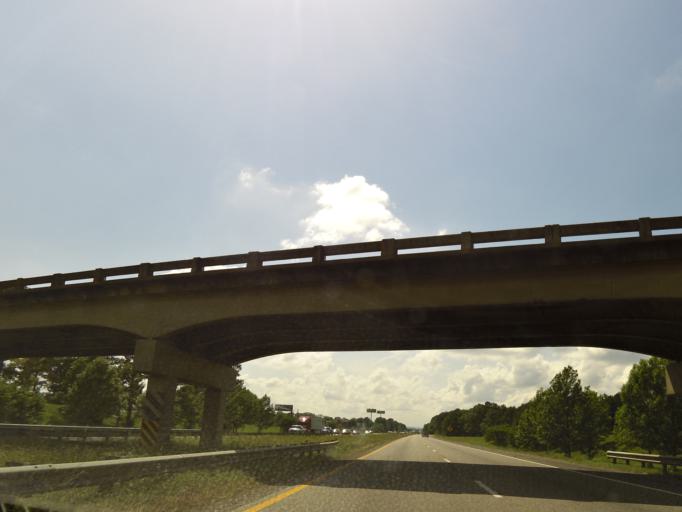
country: US
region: Alabama
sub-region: Saint Clair County
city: Riverside
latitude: 33.5916
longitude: -86.1613
